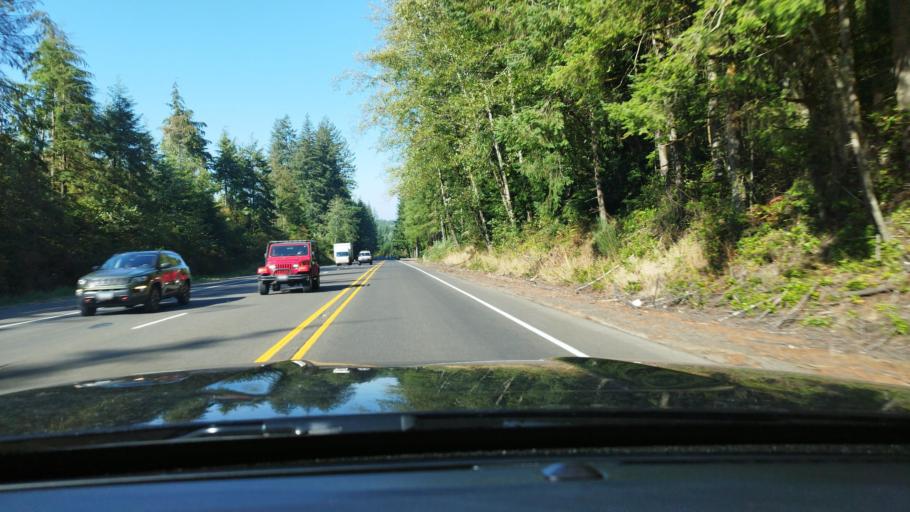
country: US
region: Washington
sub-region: Wahkiakum County
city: Cathlamet
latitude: 46.1700
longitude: -123.4631
